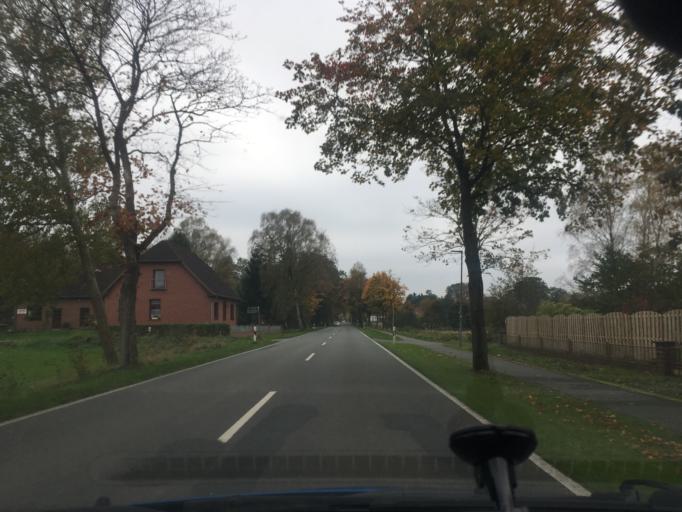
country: DE
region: Lower Saxony
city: Bispingen
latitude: 53.0895
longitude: 10.0116
